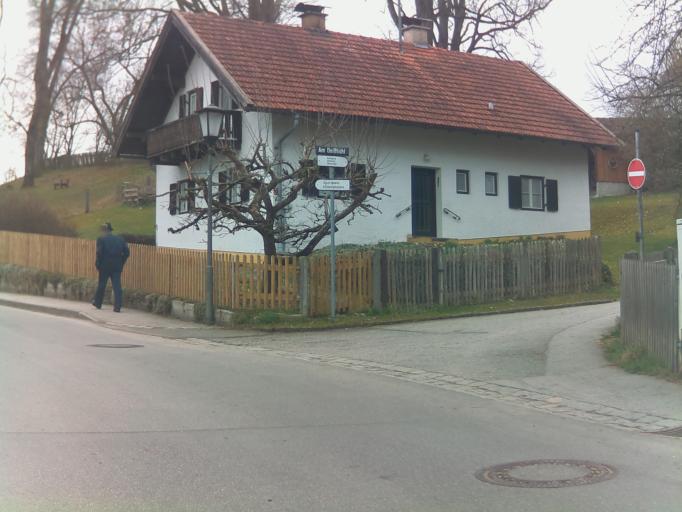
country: DE
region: Bavaria
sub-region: Upper Bavaria
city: Uffing
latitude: 47.7134
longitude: 11.1485
